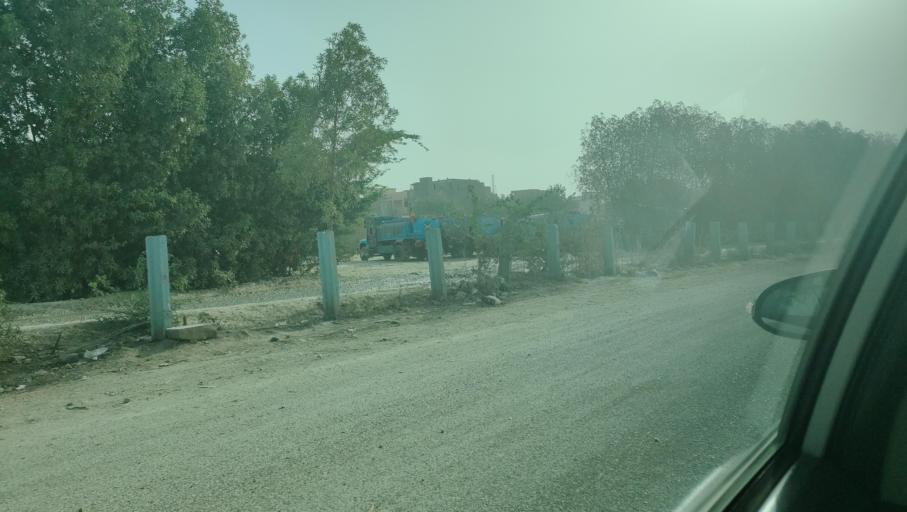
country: PK
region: Sindh
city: Malir Cantonment
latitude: 24.9383
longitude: 67.1631
